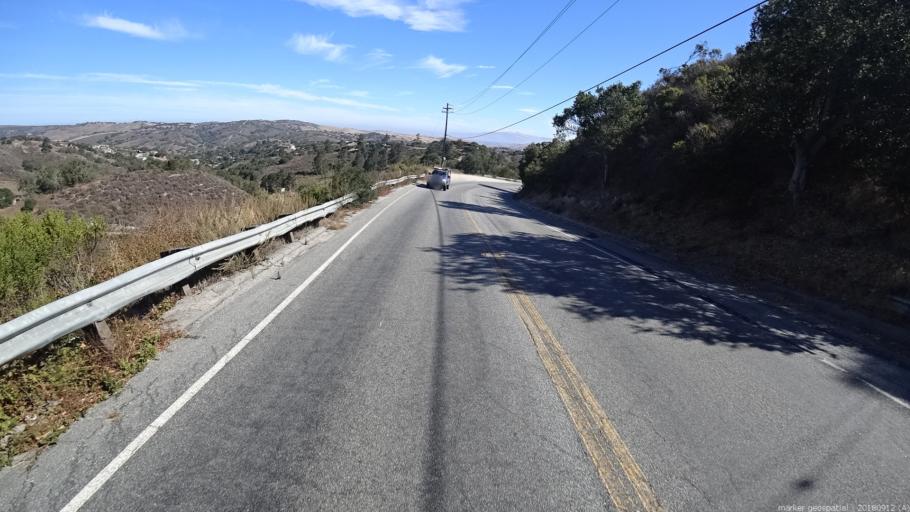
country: US
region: California
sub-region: Monterey County
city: Carmel Valley Village
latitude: 36.5557
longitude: -121.7546
